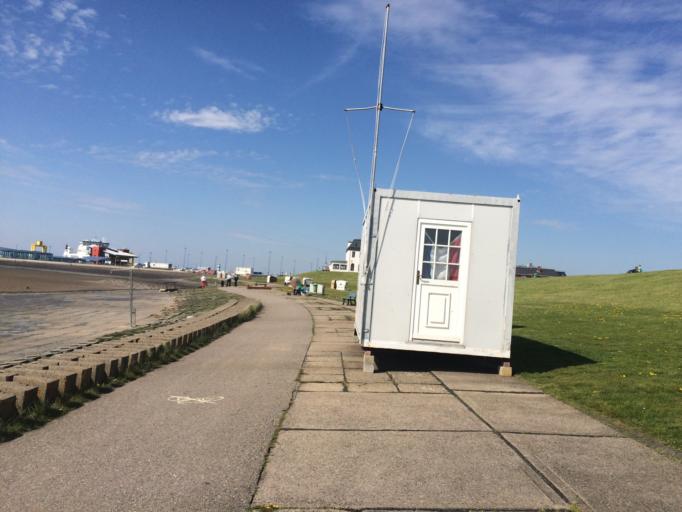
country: DE
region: Schleswig-Holstein
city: Dagebull
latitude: 54.7277
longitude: 8.6934
